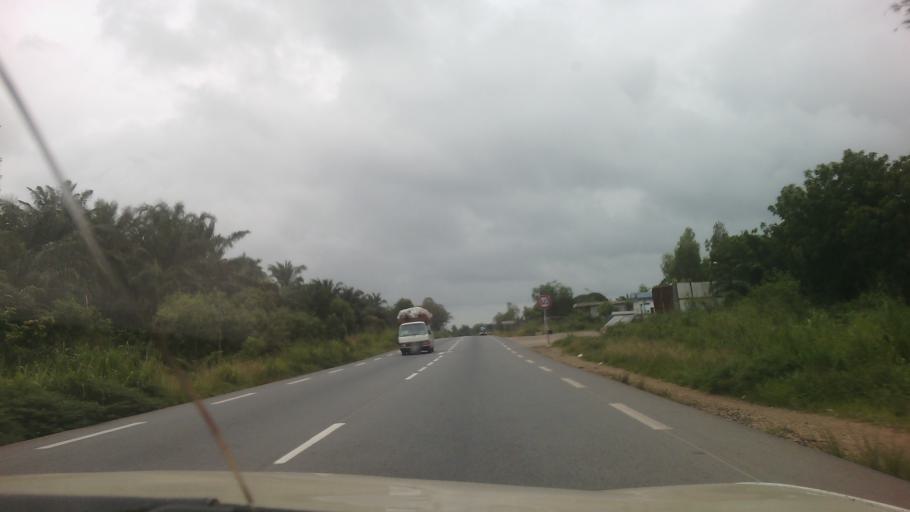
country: BJ
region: Mono
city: Come
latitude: 6.3974
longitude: 1.9794
